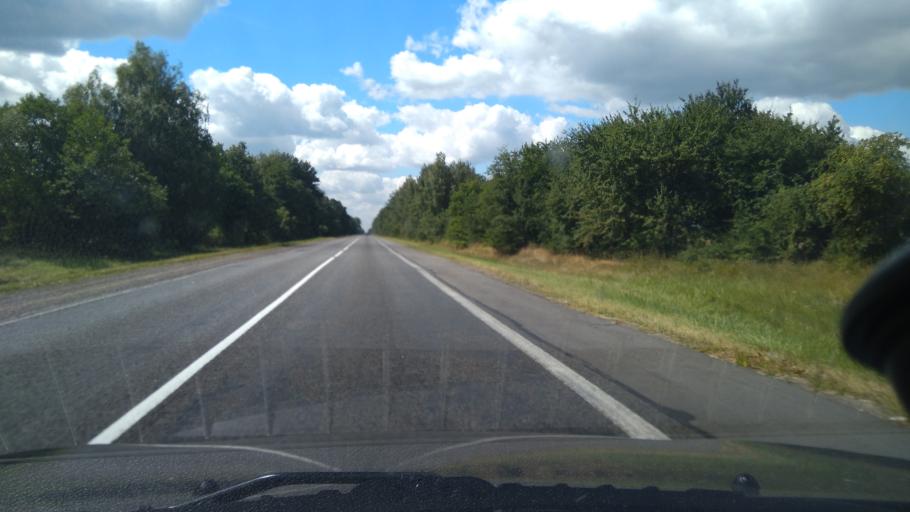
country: BY
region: Brest
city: Ivatsevichy
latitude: 52.6818
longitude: 25.2821
